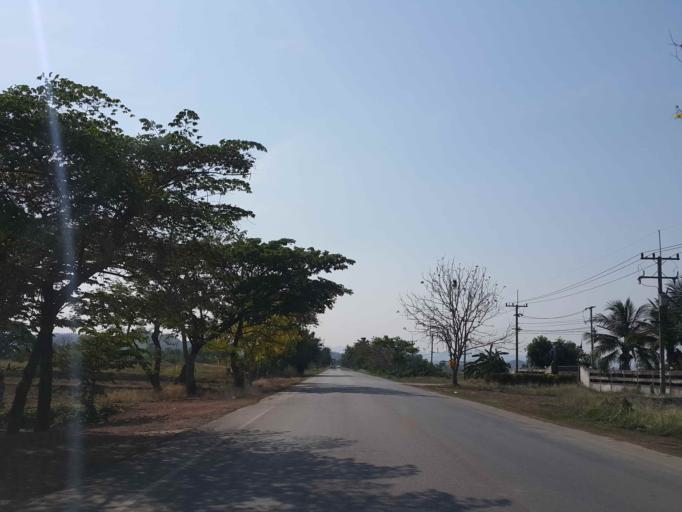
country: TH
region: Sukhothai
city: Thung Saliam
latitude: 17.3357
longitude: 99.6138
